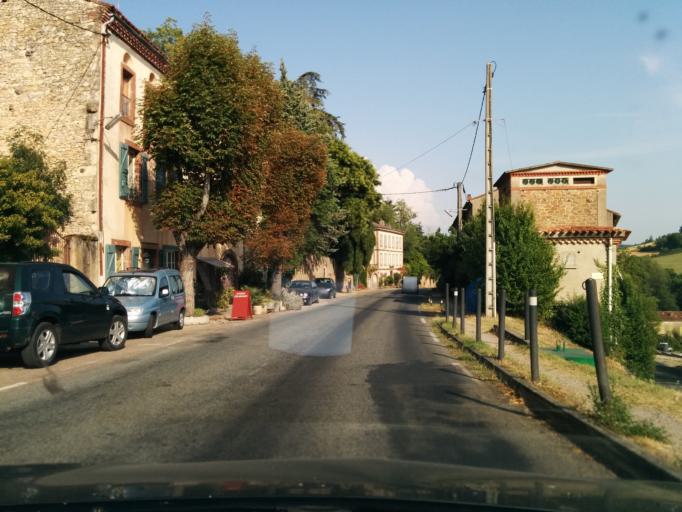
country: FR
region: Midi-Pyrenees
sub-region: Departement du Tarn
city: Cordes-sur-Ciel
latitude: 44.0615
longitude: 1.9592
